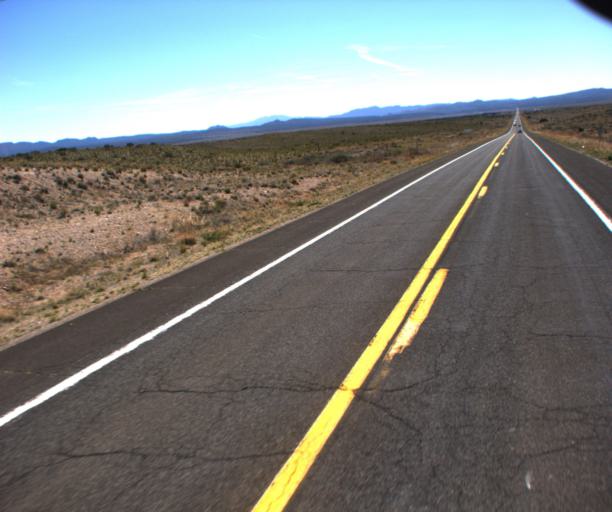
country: US
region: Arizona
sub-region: Mohave County
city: Peach Springs
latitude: 35.5164
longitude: -113.4981
